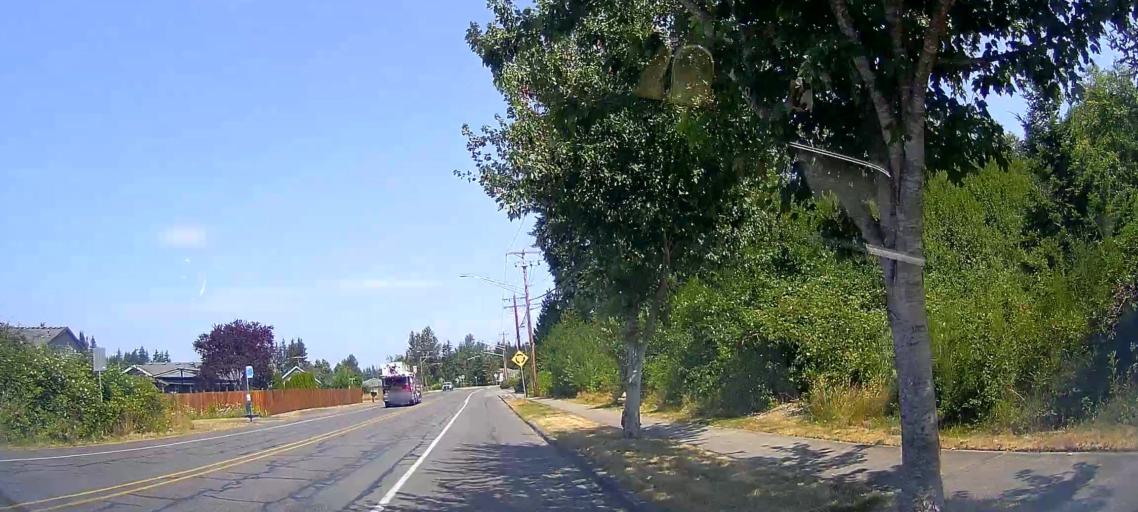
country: US
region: Washington
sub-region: Snohomish County
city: Marysville
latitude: 48.0914
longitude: -122.1641
